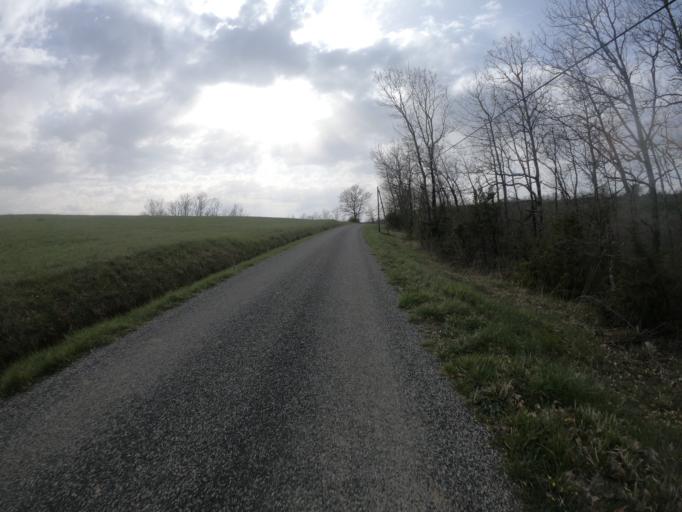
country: FR
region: Languedoc-Roussillon
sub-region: Departement de l'Aude
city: Belpech
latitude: 43.1288
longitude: 1.7447
